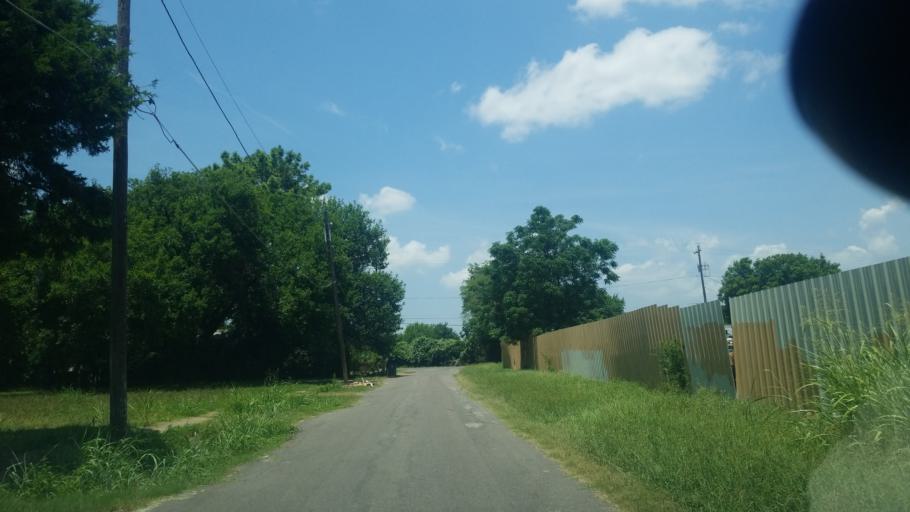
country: US
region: Texas
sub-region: Dallas County
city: Dallas
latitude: 32.7431
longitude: -96.7832
